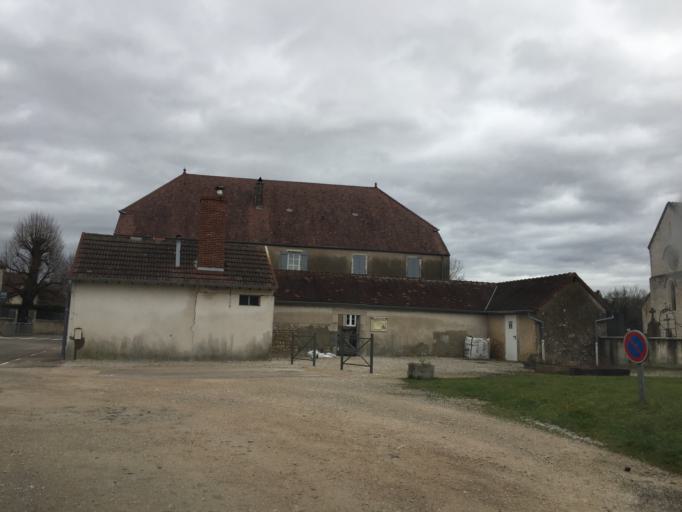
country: FR
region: Franche-Comte
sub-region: Departement du Doubs
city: Arc-et-Senans
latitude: 47.0213
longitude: 5.7199
